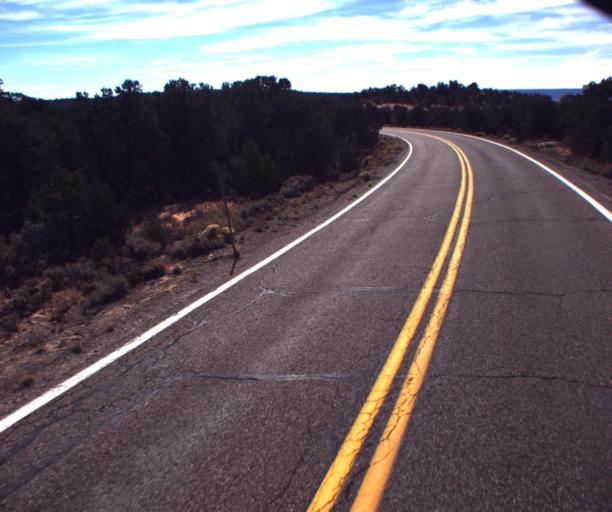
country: US
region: Arizona
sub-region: Navajo County
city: Kayenta
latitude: 36.6603
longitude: -110.5272
